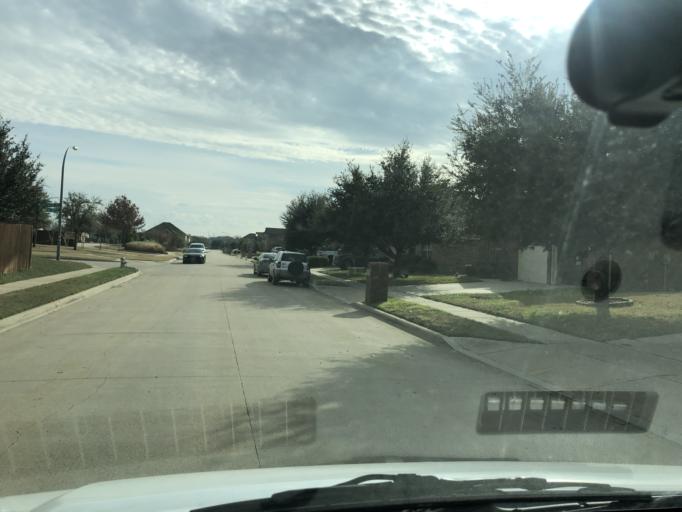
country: US
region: Texas
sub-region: Tarrant County
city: Saginaw
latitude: 32.9130
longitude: -97.3735
